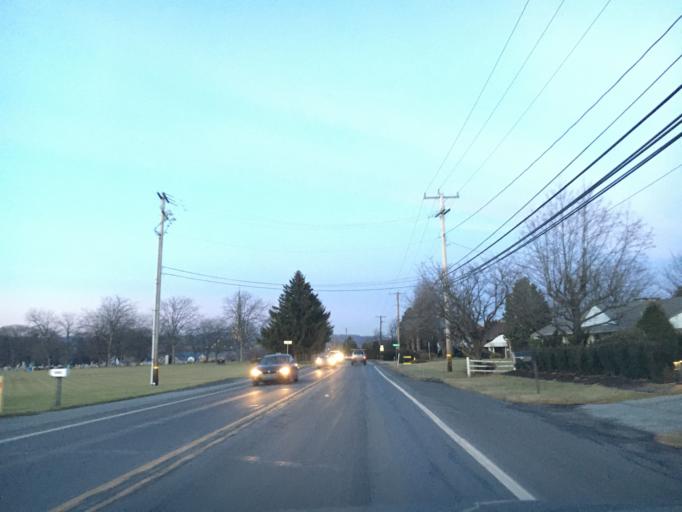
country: US
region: Pennsylvania
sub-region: Lehigh County
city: Schnecksville
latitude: 40.6880
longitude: -75.6104
